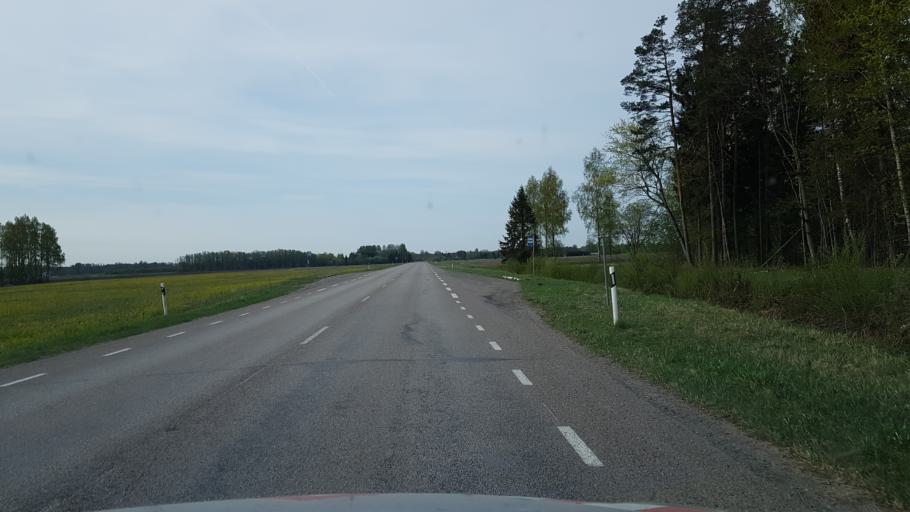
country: EE
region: Paernumaa
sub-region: Audru vald
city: Audru
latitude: 58.3811
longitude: 24.2717
